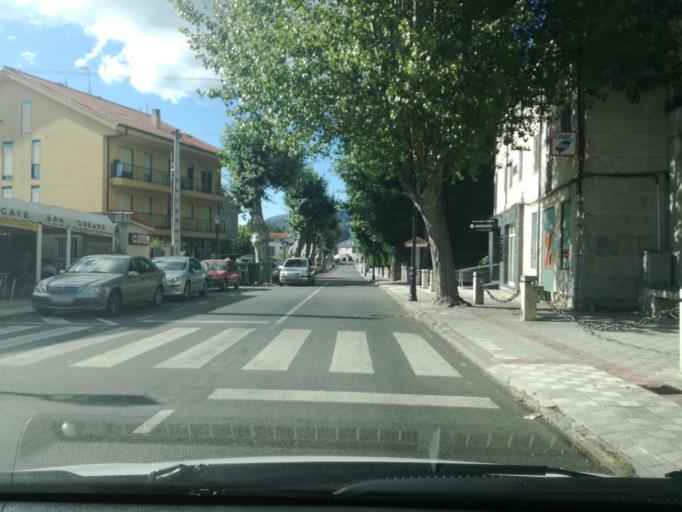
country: ES
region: Galicia
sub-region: Provincia de Ourense
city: Lobios
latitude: 41.8997
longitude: -8.0831
